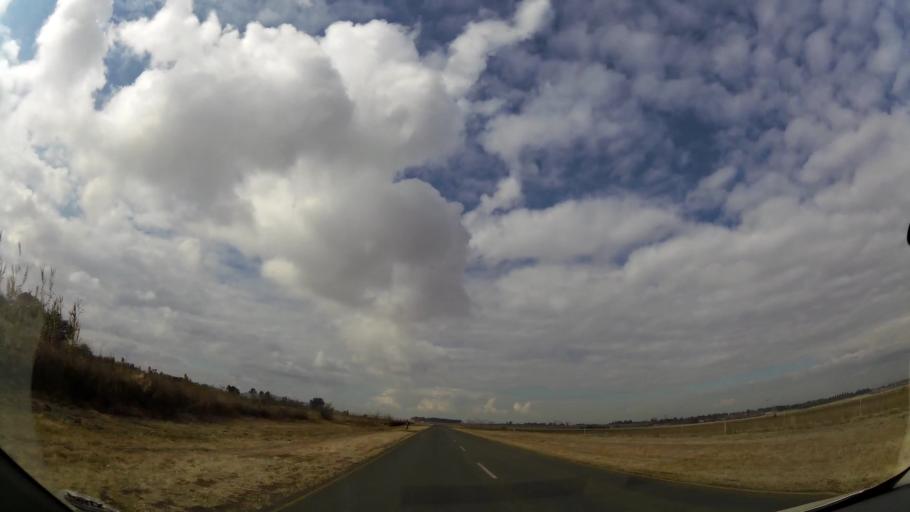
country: ZA
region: Gauteng
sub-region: Sedibeng District Municipality
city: Meyerton
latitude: -26.6153
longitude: 28.0527
